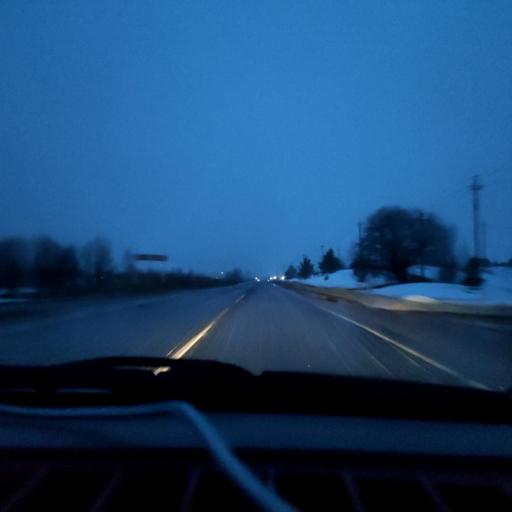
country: RU
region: Perm
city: Ust'-Kachka
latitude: 57.9491
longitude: 55.7369
